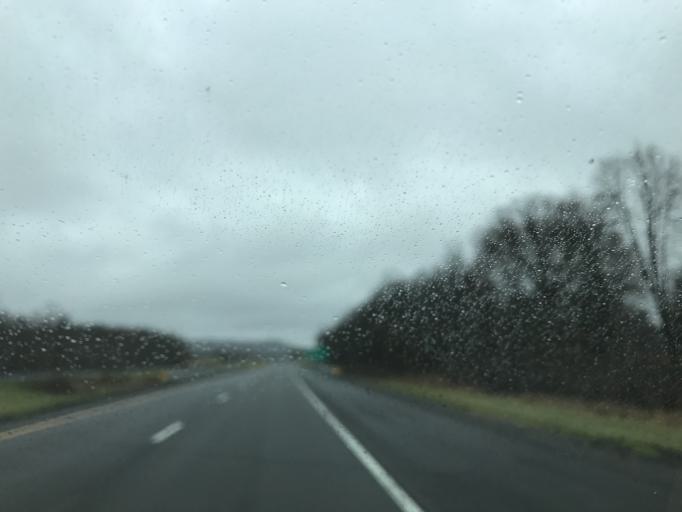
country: US
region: West Virginia
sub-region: Greenbrier County
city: Rainelle
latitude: 37.9015
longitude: -80.6406
